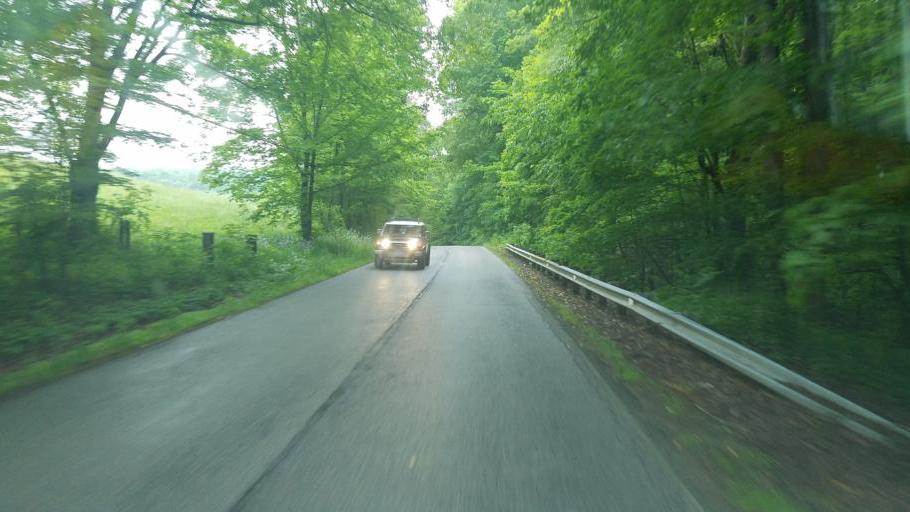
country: US
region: Ohio
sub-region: Richland County
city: Lincoln Heights
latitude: 40.6916
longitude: -82.4395
